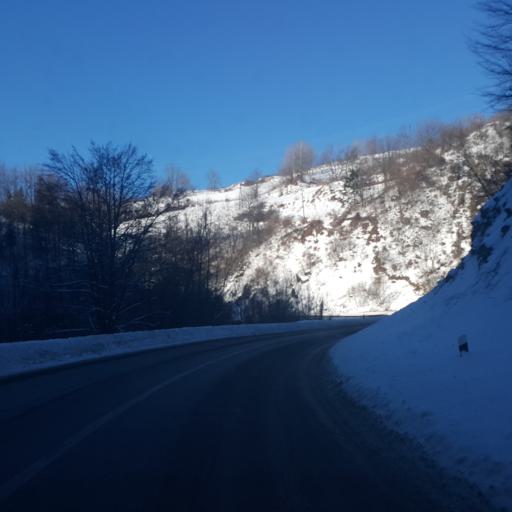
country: RS
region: Central Serbia
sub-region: Rasinski Okrug
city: Aleksandrovac
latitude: 43.3044
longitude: 20.9003
